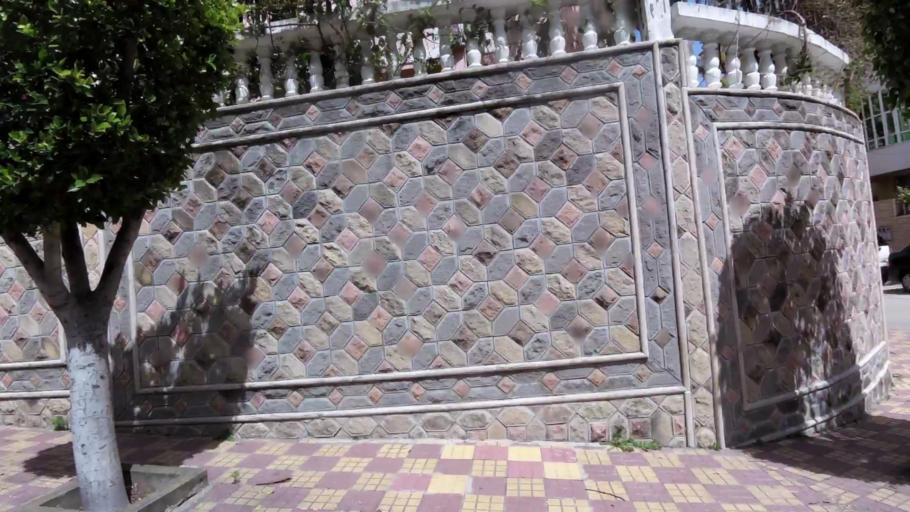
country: MA
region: Tanger-Tetouan
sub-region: Tanger-Assilah
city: Tangier
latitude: 35.7584
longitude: -5.8369
